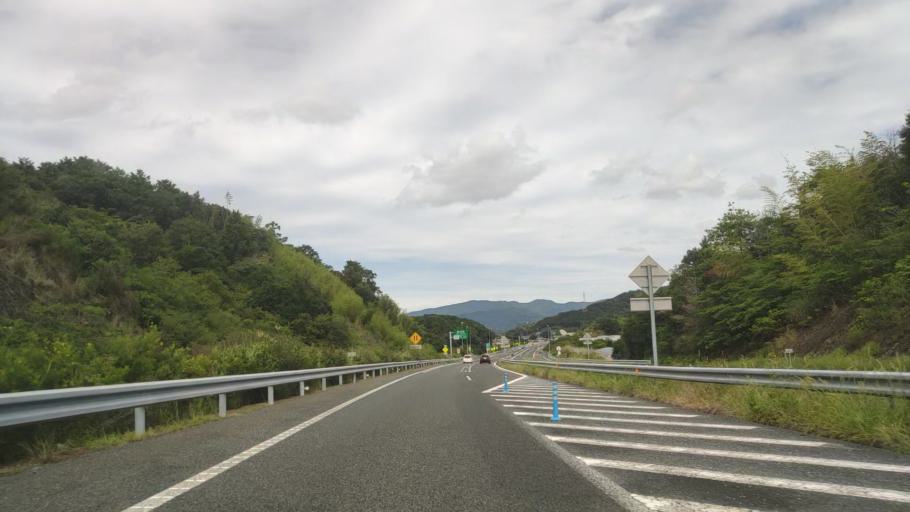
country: JP
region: Wakayama
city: Gobo
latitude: 33.8834
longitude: 135.1829
